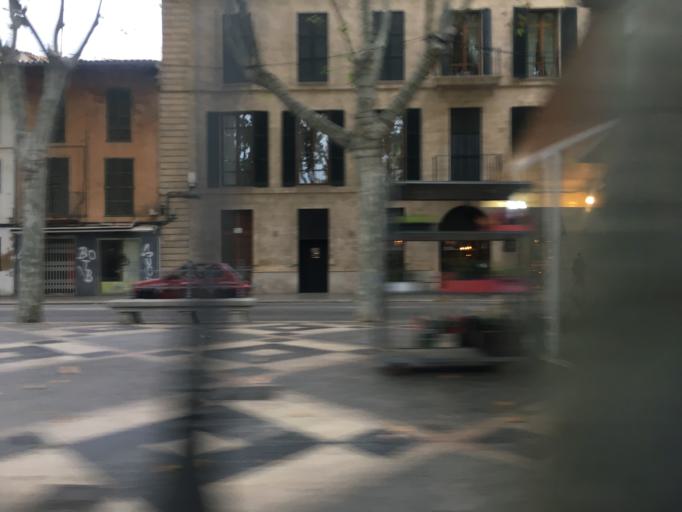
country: ES
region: Balearic Islands
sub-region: Illes Balears
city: Palma
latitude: 39.5746
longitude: 2.6484
